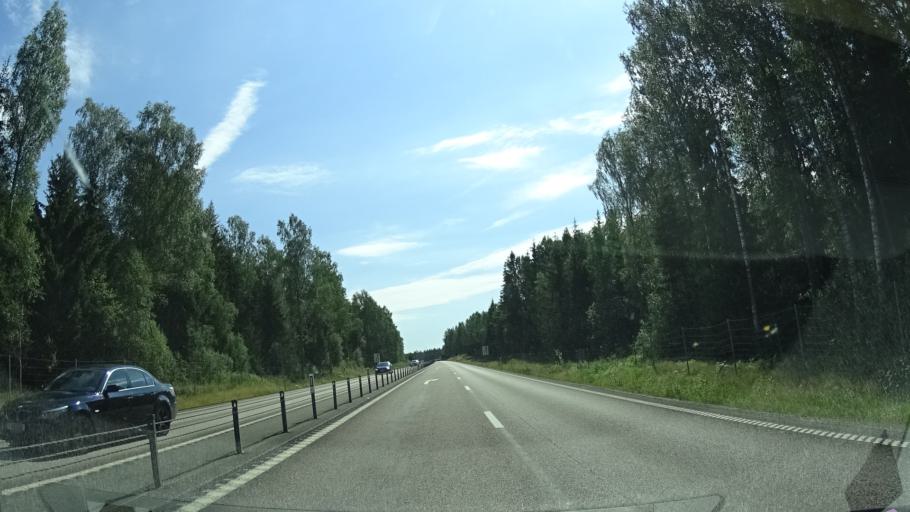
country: SE
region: Vaermland
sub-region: Kristinehamns Kommun
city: Kristinehamn
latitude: 59.3665
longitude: 14.0197
